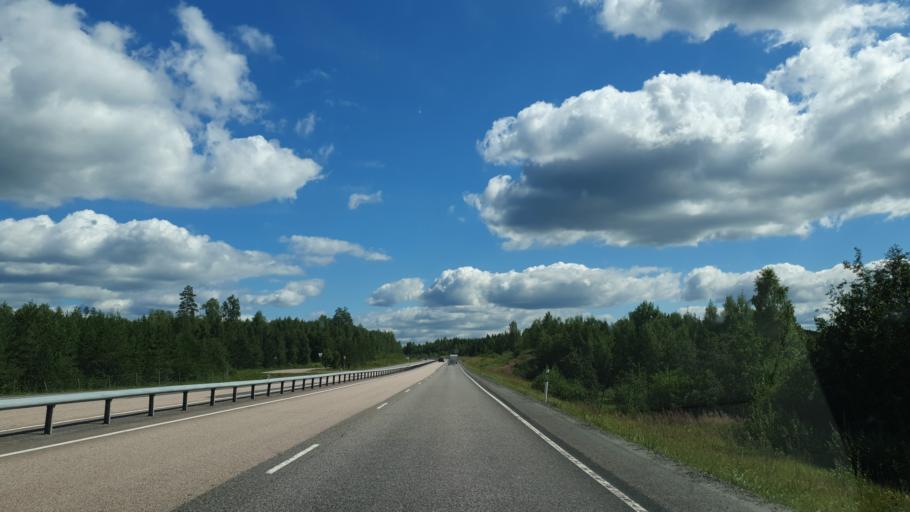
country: FI
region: Pirkanmaa
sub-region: Tampere
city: Orivesi
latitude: 61.7085
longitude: 24.5373
